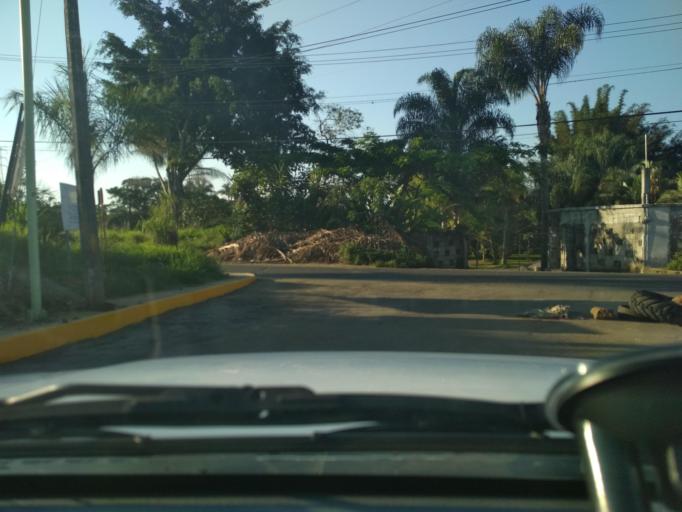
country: MX
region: Veracruz
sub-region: Fortin
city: Fraccionamiento Villas de la Llave
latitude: 18.9152
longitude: -96.9962
